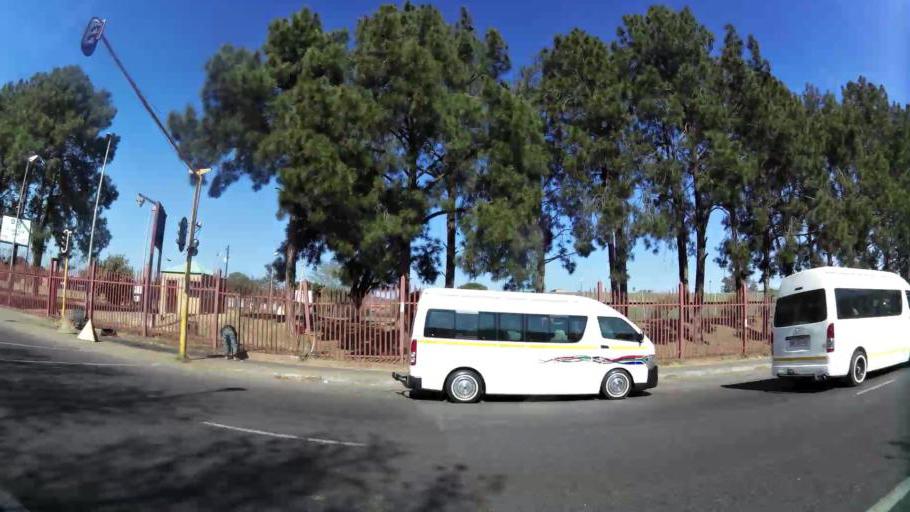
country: ZA
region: Gauteng
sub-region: City of Tshwane Metropolitan Municipality
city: Pretoria
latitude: -25.7479
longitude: 28.1672
